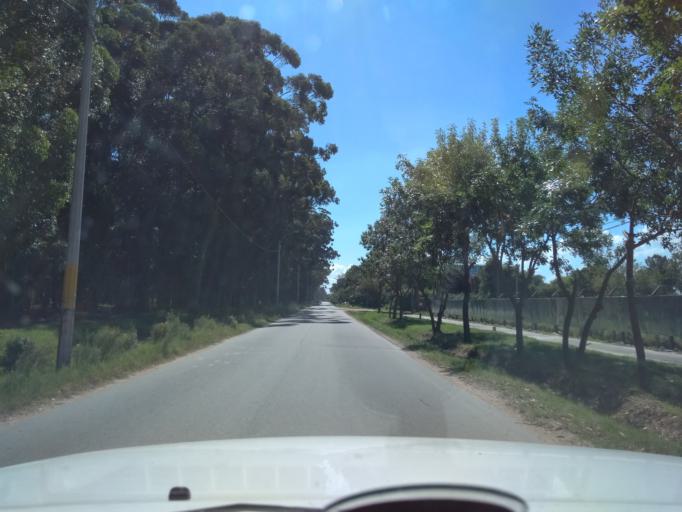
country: UY
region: Canelones
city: Barra de Carrasco
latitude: -34.8548
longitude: -56.0205
